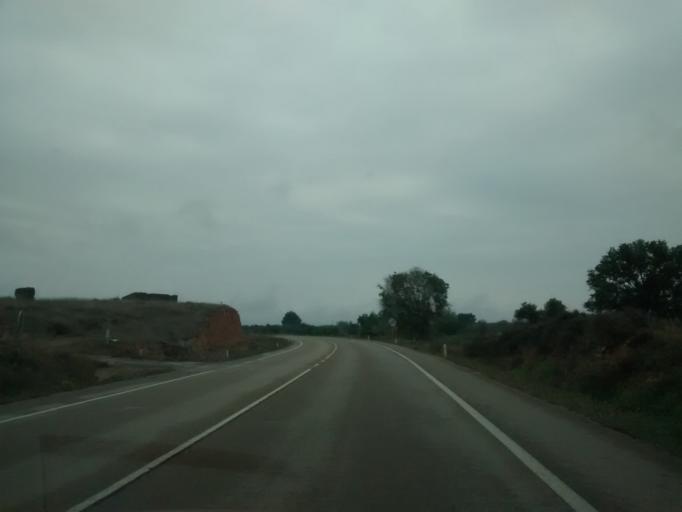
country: ES
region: Aragon
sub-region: Provincia de Zaragoza
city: Caspe
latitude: 41.2212
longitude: -0.0199
